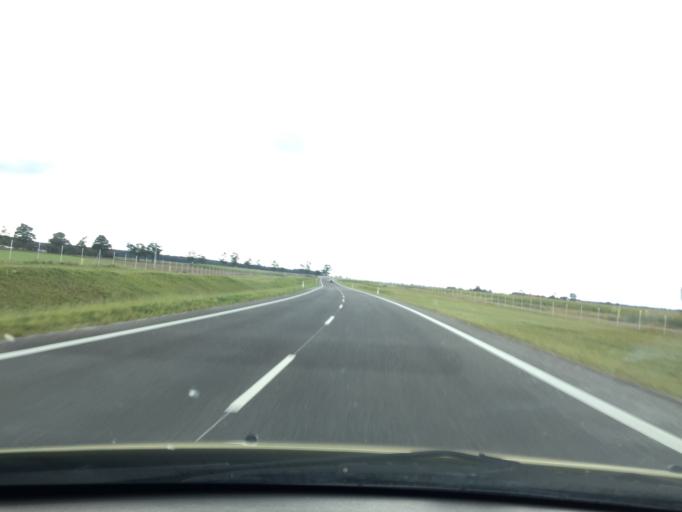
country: PL
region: Greater Poland Voivodeship
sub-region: Powiat sredzki
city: Nowe Miasto nad Warta
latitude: 52.0445
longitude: 17.4544
